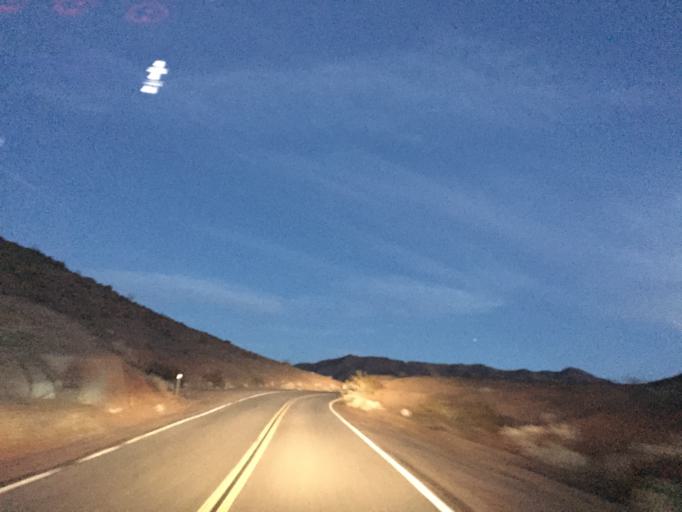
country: US
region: California
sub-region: San Bernardino County
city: Fort Irwin
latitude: 35.9104
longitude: -116.5803
